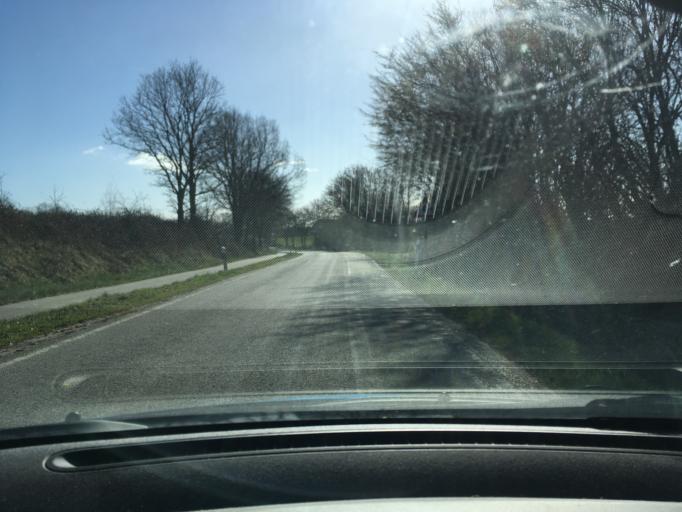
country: DE
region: Schleswig-Holstein
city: Fahrdorf
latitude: 54.5039
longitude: 9.6290
